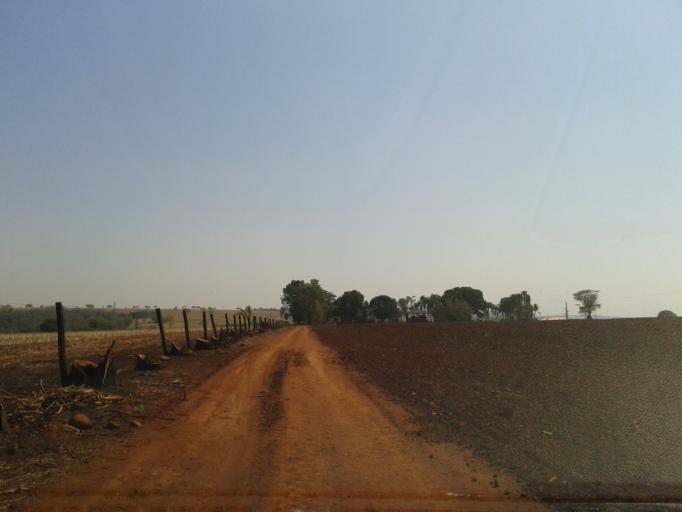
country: BR
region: Minas Gerais
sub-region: Ituiutaba
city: Ituiutaba
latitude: -18.9534
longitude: -49.4510
